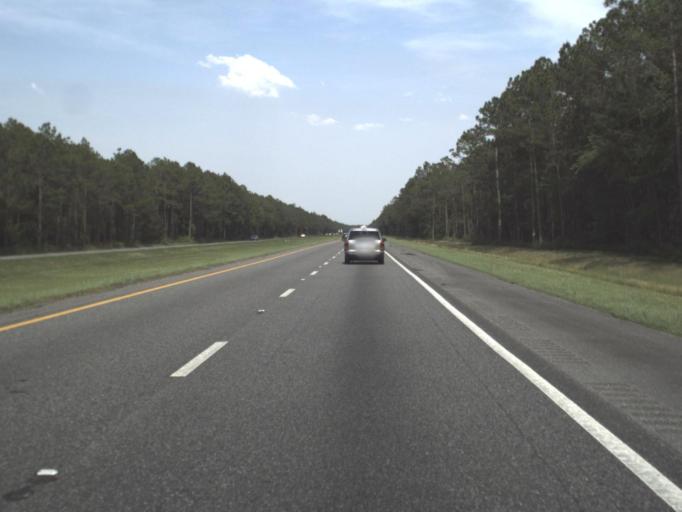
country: US
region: Florida
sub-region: Union County
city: Lake Butler
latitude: 30.2541
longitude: -82.3625
